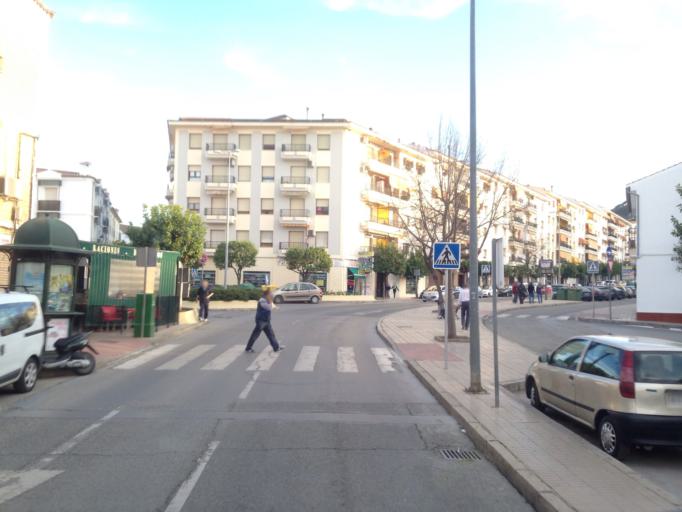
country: ES
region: Andalusia
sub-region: Provincia de Malaga
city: Antequera
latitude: 37.0192
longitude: -4.5651
